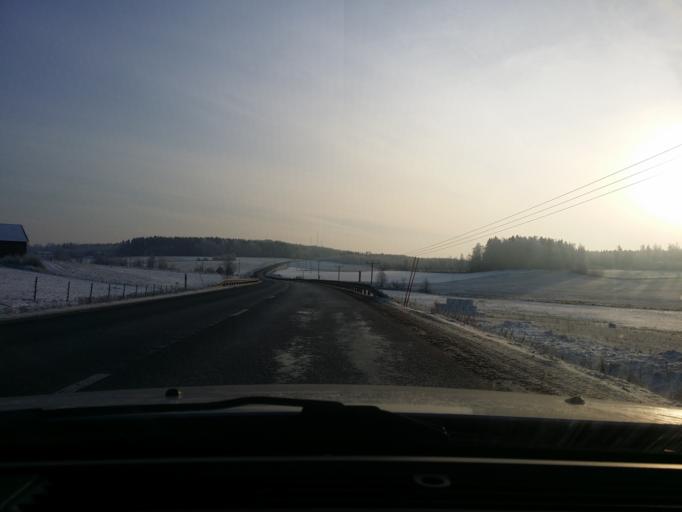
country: SE
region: OErebro
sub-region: Lindesbergs Kommun
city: Lindesberg
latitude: 59.5895
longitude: 15.1880
